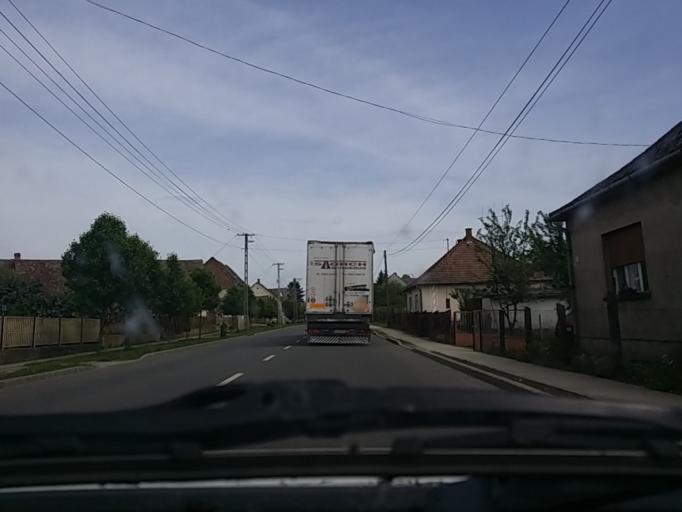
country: HU
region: Baranya
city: Sellye
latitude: 45.8818
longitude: 17.9025
